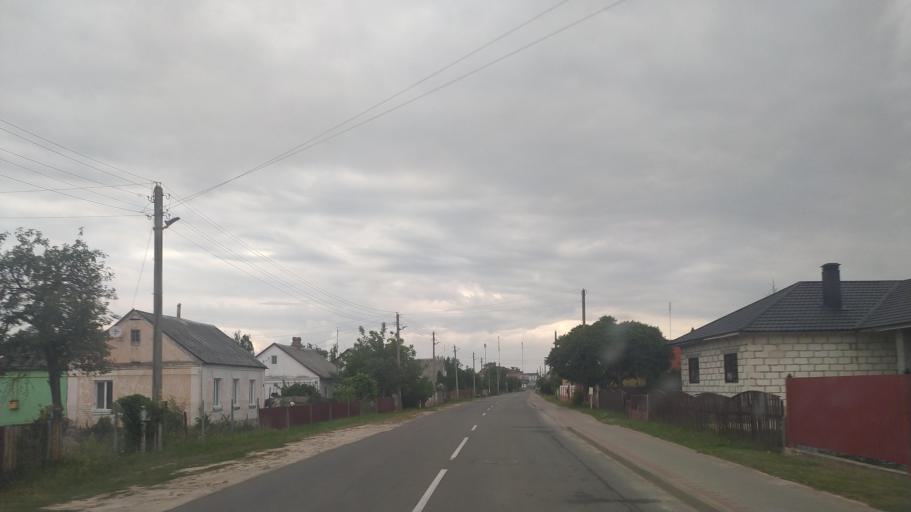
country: BY
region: Brest
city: Byaroza
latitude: 52.5243
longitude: 24.9737
